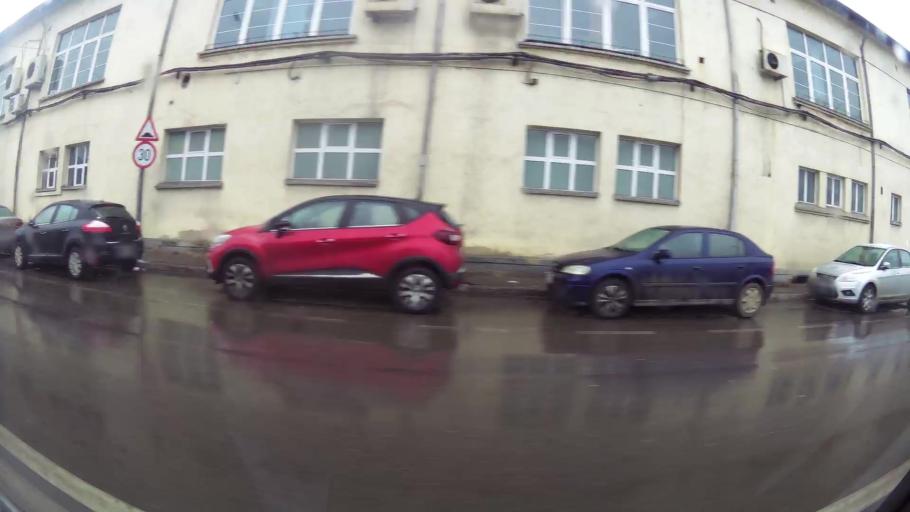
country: RO
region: Prahova
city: Ploiesti
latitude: 44.9557
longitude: 26.0150
